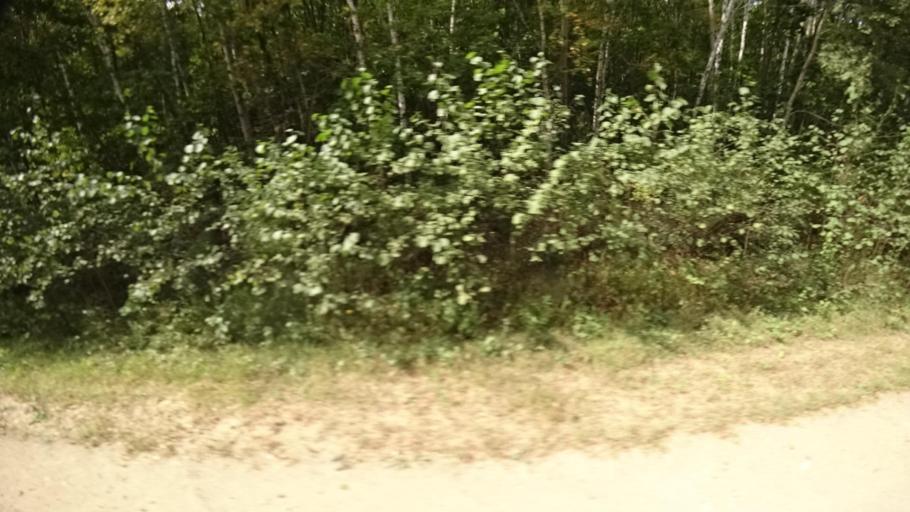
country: RU
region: Primorskiy
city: Yakovlevka
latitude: 44.6731
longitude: 133.6119
